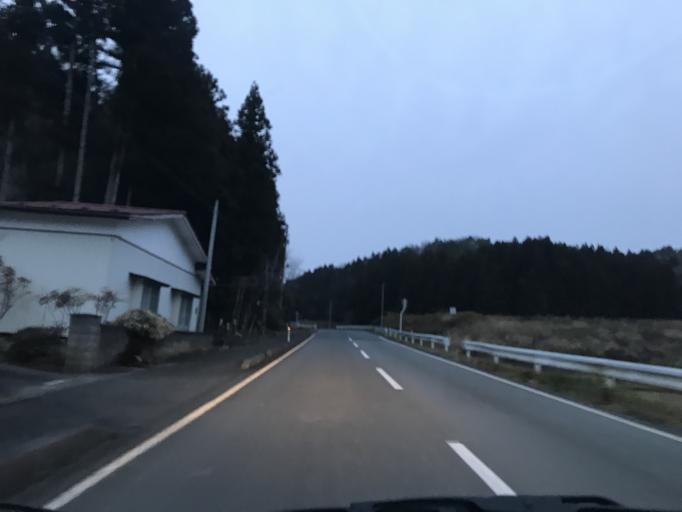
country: JP
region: Iwate
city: Ichinoseki
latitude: 38.8160
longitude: 141.1162
